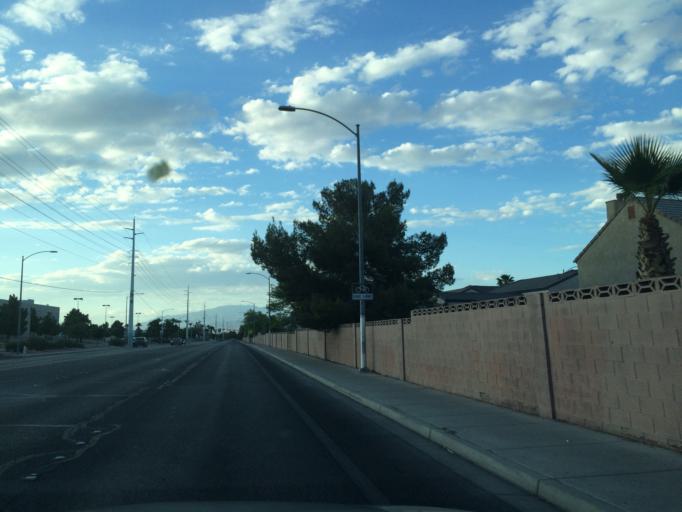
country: US
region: Nevada
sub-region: Clark County
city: Spring Valley
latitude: 36.2001
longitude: -115.2513
